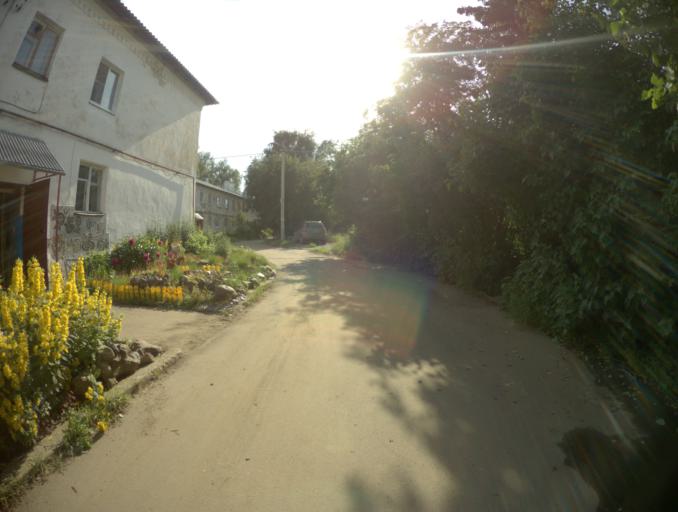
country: RU
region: Vladimir
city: Suzdal'
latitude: 56.4253
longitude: 40.4535
